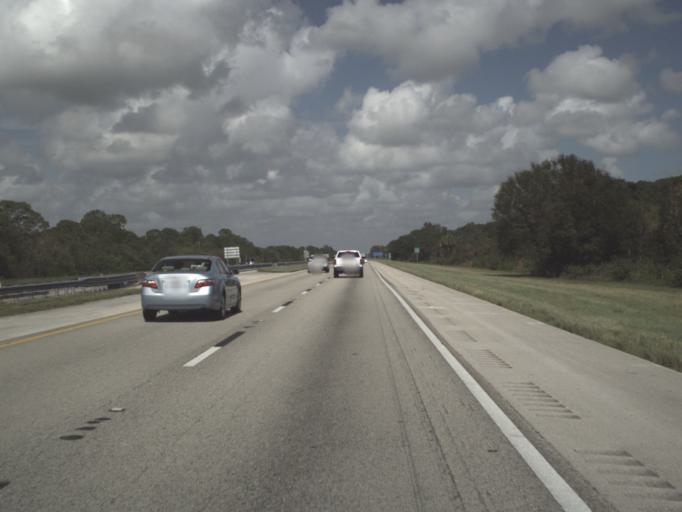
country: US
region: Florida
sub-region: Saint Lucie County
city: Fort Pierce South
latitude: 27.4203
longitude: -80.4076
